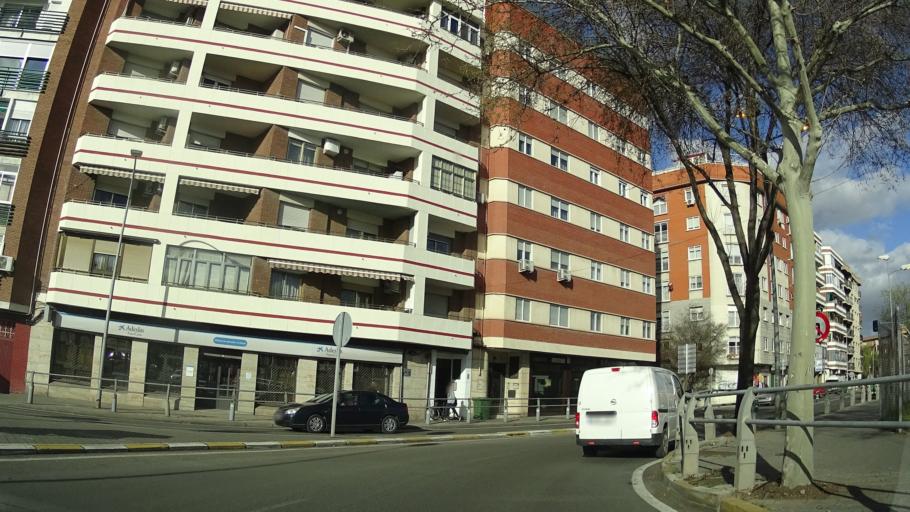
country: ES
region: Castille-La Mancha
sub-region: Provincia de Ciudad Real
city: Ciudad Real
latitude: 38.9799
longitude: -3.9289
